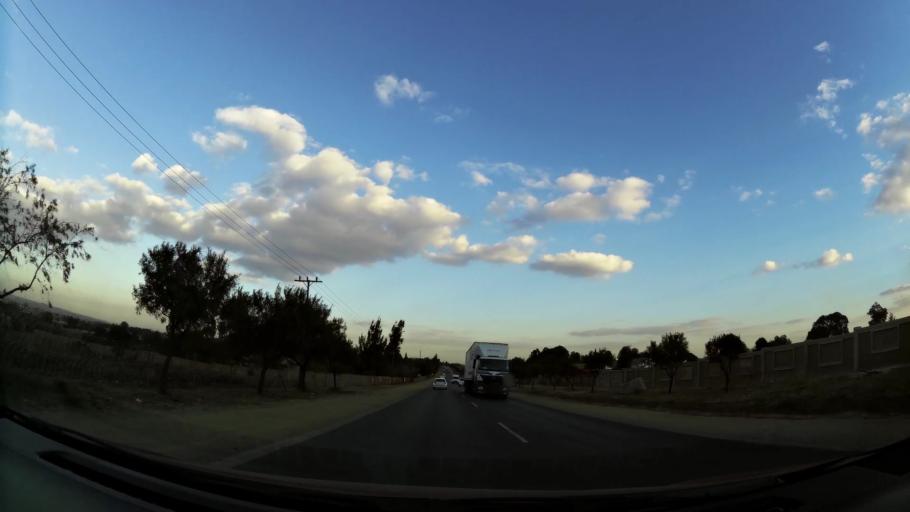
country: ZA
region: Gauteng
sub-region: City of Johannesburg Metropolitan Municipality
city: Midrand
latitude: -25.9963
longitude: 28.1553
